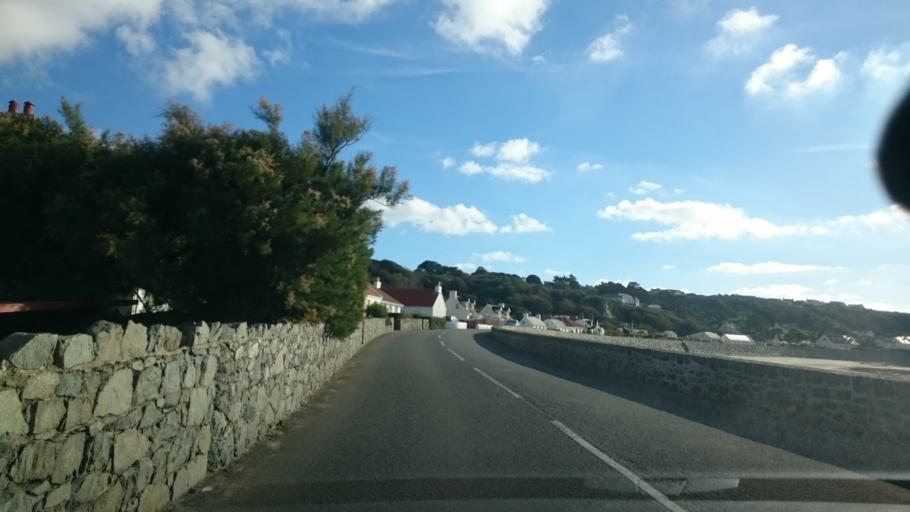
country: GG
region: St Peter Port
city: Saint Peter Port
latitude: 49.4388
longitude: -2.6535
